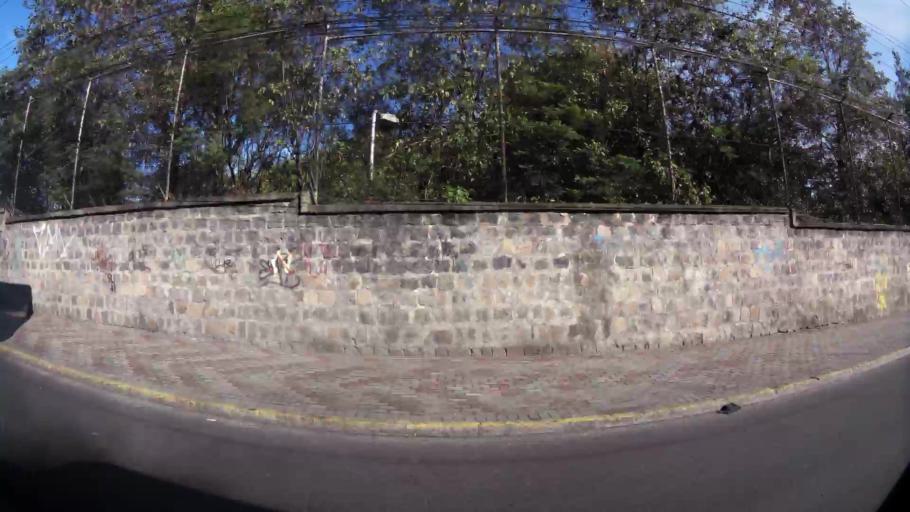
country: EC
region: Pichincha
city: Quito
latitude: -0.2717
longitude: -78.5291
